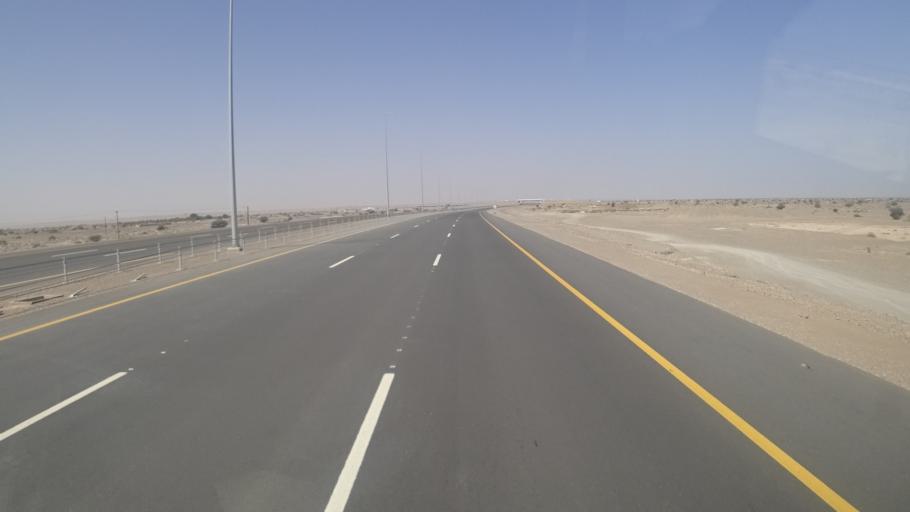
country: OM
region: Ash Sharqiyah
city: Badiyah
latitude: 22.2776
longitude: 59.1794
